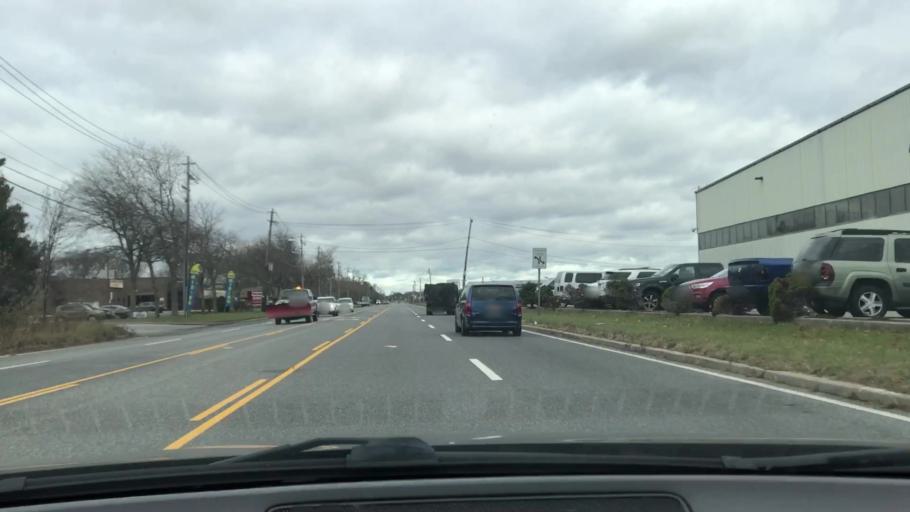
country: US
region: New York
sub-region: Suffolk County
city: Ronkonkoma
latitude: 40.7952
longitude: -73.1107
